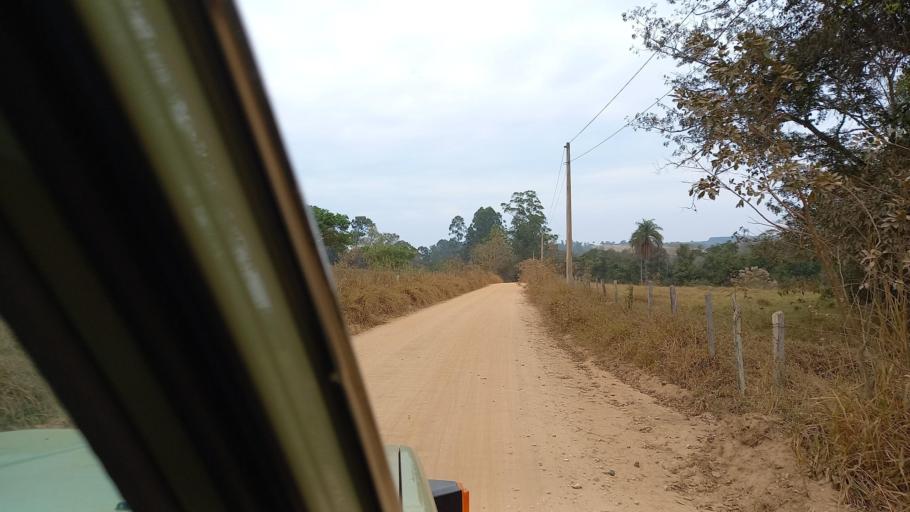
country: BR
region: Sao Paulo
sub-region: Moji-Guacu
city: Mogi-Gaucu
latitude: -22.3052
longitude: -46.8327
